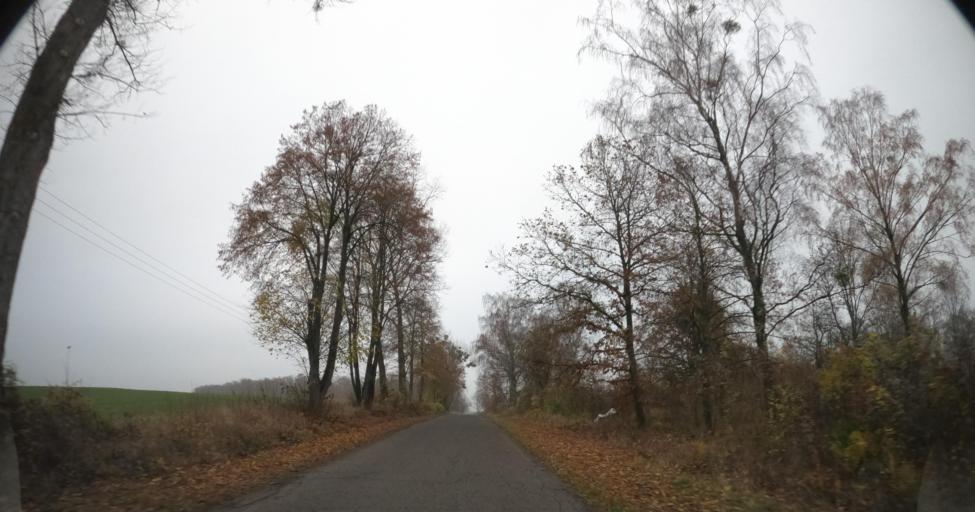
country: PL
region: West Pomeranian Voivodeship
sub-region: Powiat lobeski
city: Wegorzyno
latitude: 53.5429
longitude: 15.6433
